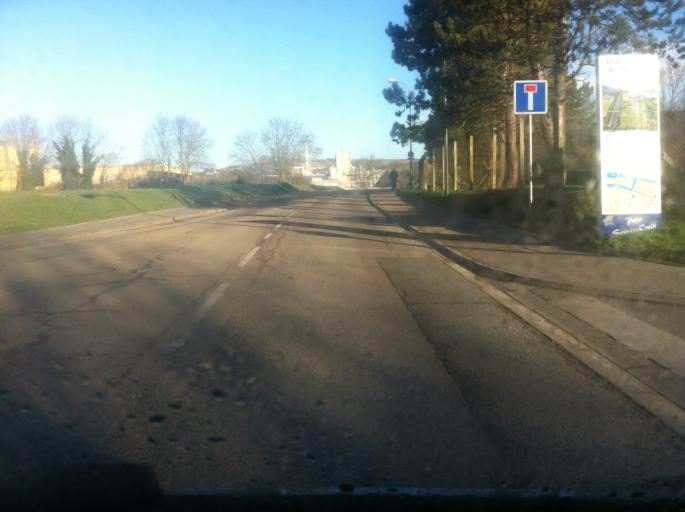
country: FR
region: Picardie
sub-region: Departement de la Somme
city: Mers-les-Bains
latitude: 50.0581
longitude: 1.3882
